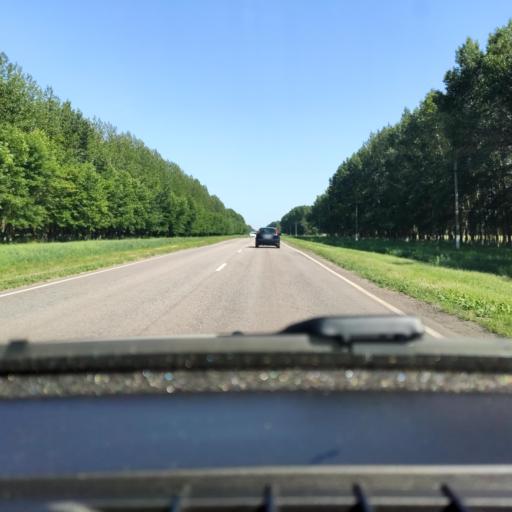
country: RU
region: Voronezj
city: Panino
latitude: 51.6653
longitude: 39.9723
